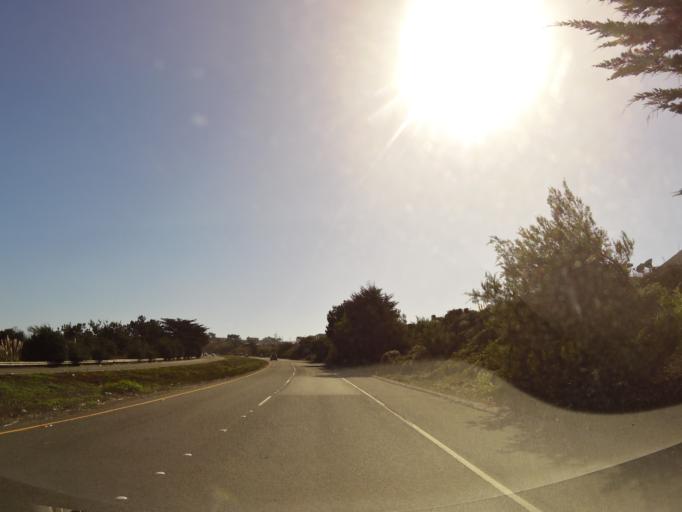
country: US
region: California
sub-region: San Mateo County
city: Broadmoor
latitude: 37.6781
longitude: -122.4904
